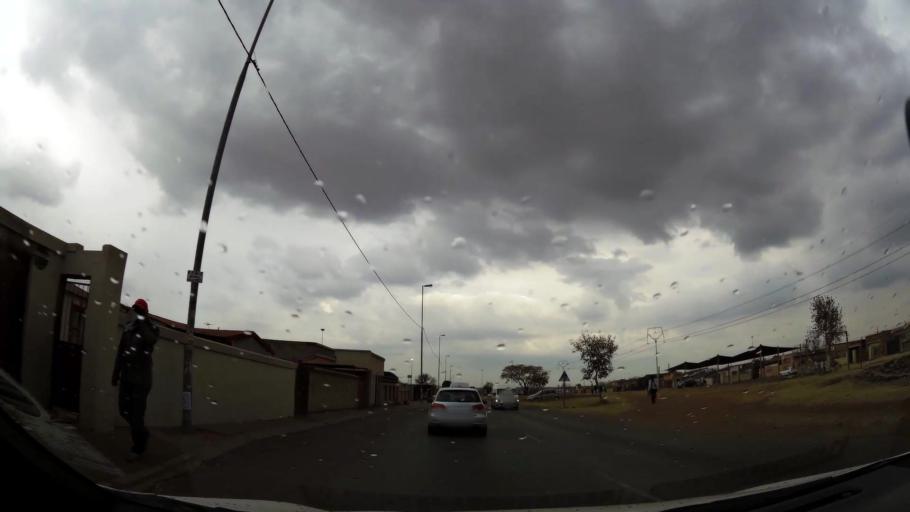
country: ZA
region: Gauteng
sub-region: Ekurhuleni Metropolitan Municipality
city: Germiston
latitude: -26.3568
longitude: 28.1441
